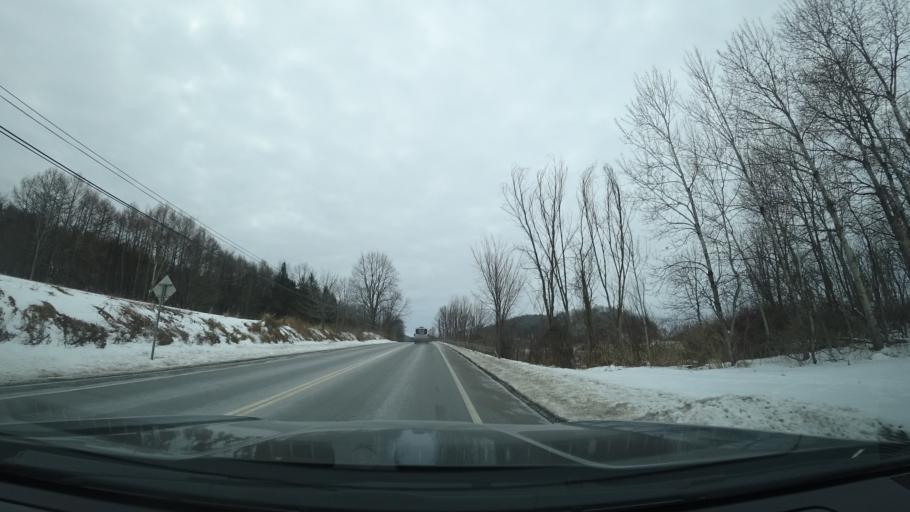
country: US
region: New York
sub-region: Washington County
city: Greenwich
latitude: 43.2033
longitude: -73.4863
